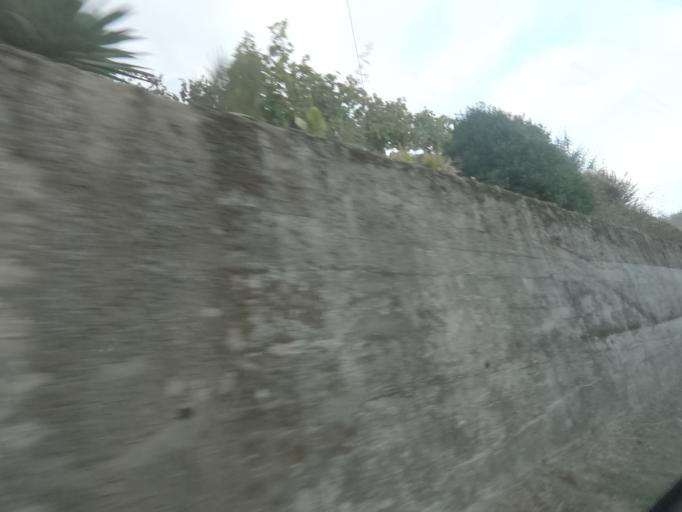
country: PT
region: Vila Real
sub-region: Mesao Frio
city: Mesao Frio
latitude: 41.1681
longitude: -7.8763
